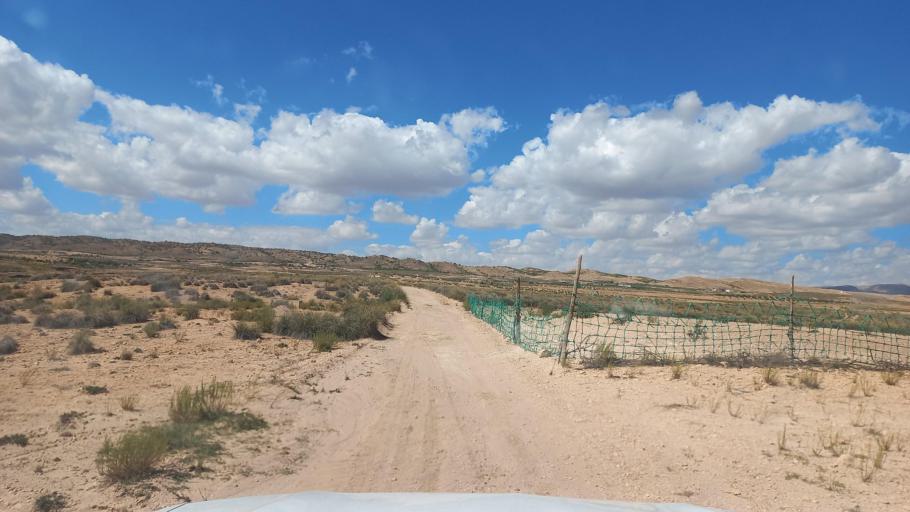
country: TN
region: Al Qasrayn
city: Sbiba
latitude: 35.3562
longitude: 9.0105
